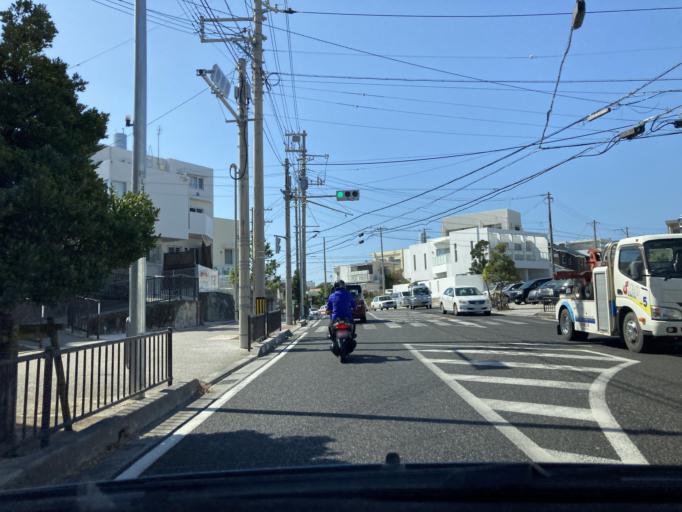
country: JP
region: Okinawa
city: Naha-shi
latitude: 26.2297
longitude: 127.7196
